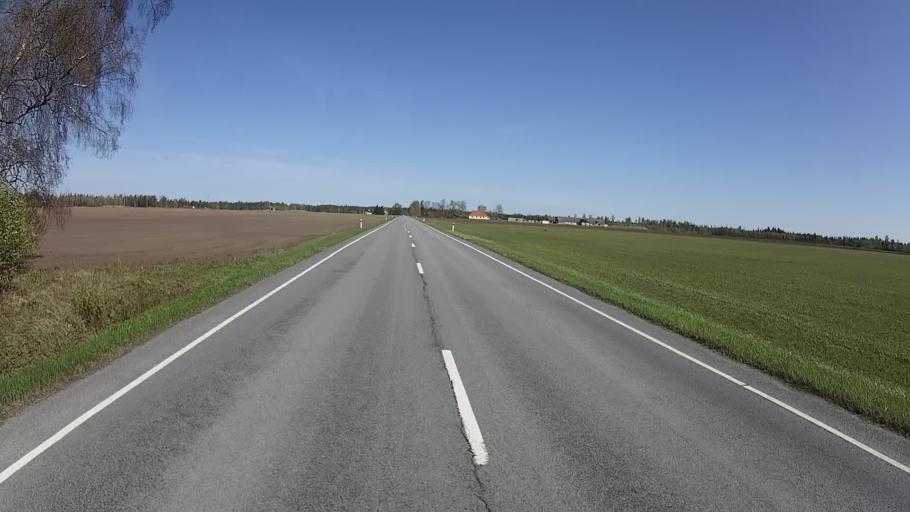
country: EE
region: Raplamaa
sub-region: Jaervakandi vald
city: Jarvakandi
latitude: 58.8364
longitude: 24.7969
